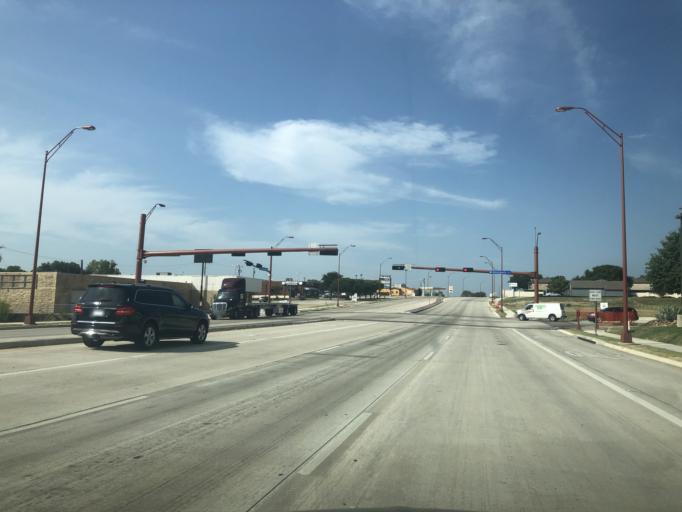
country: US
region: Texas
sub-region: Tarrant County
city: Benbrook
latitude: 32.6719
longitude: -97.4709
